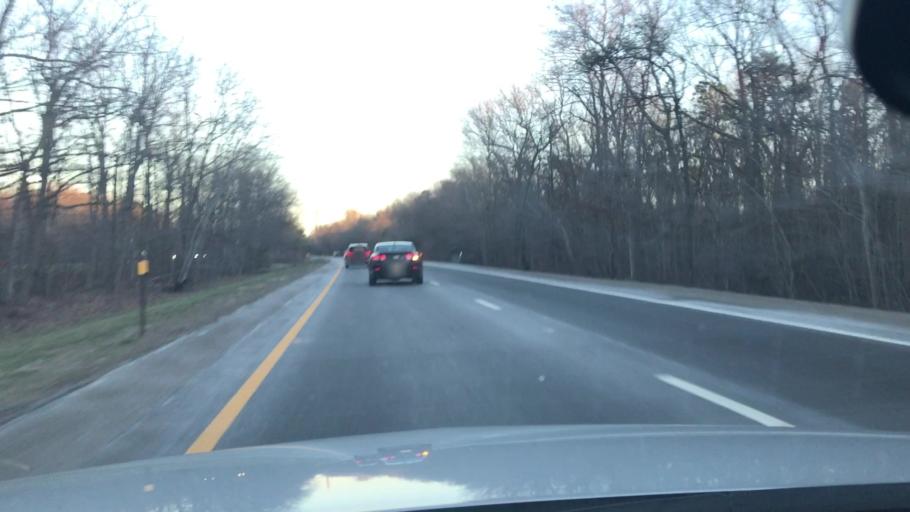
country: US
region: New Jersey
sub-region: Camden County
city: Sicklerville
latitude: 39.7215
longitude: -74.9973
